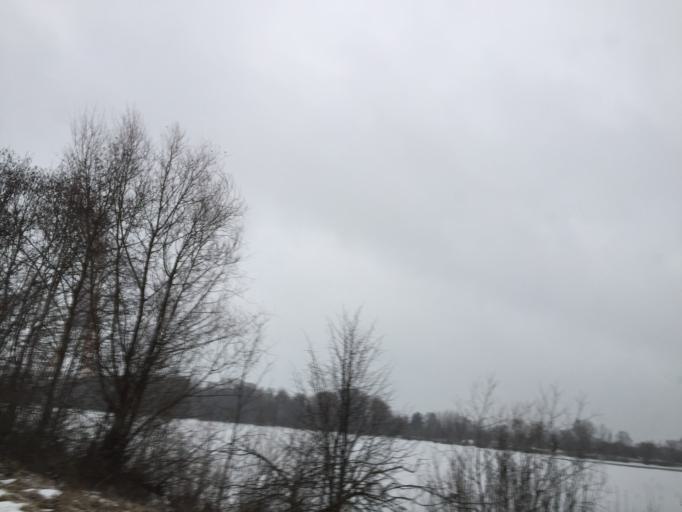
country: LV
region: Riga
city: Riga
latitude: 56.9178
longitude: 24.1422
